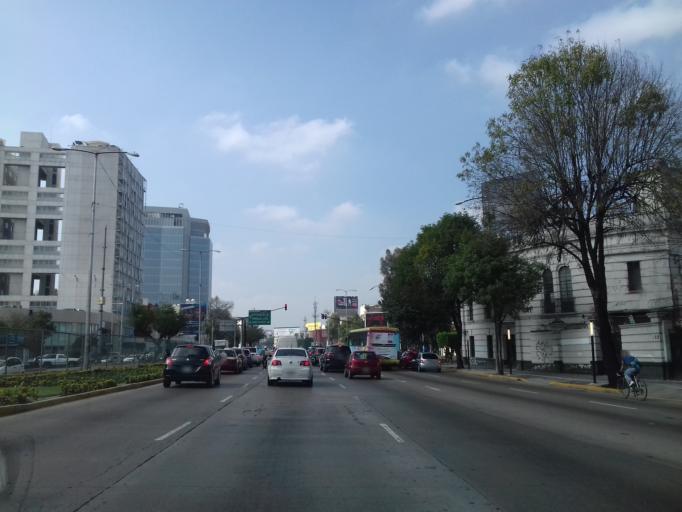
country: MX
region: Mexico City
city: Polanco
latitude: 19.4121
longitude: -99.1819
